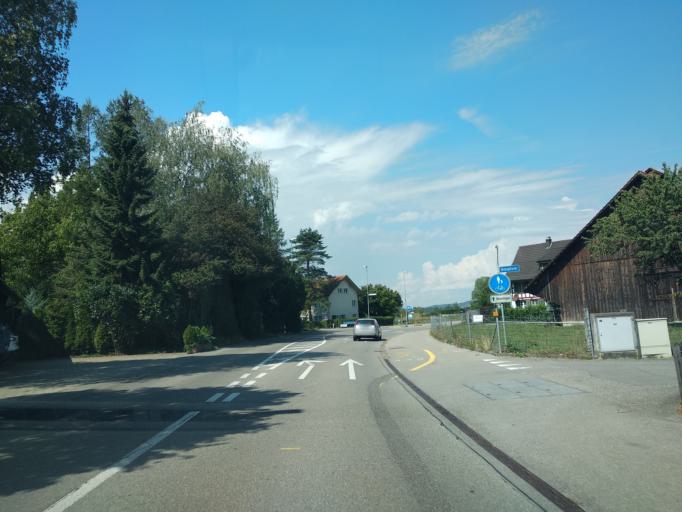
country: CH
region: Thurgau
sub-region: Frauenfeld District
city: Gachnang
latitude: 47.5692
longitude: 8.8439
